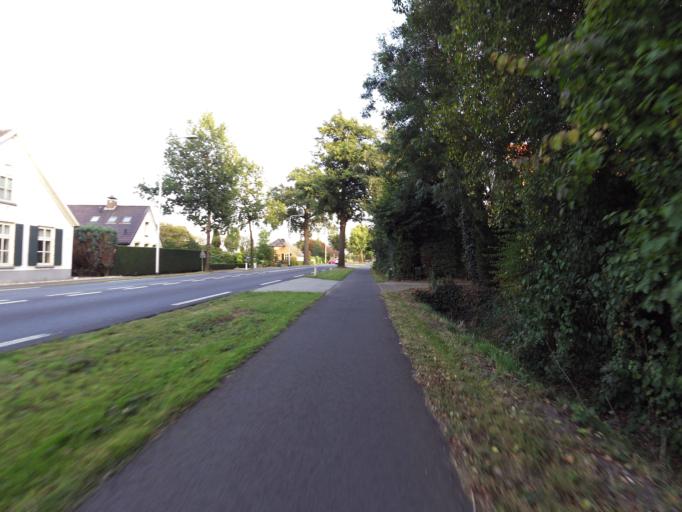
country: NL
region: Gelderland
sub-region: Gemeente Zevenaar
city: Zevenaar
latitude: 51.9114
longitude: 6.1024
